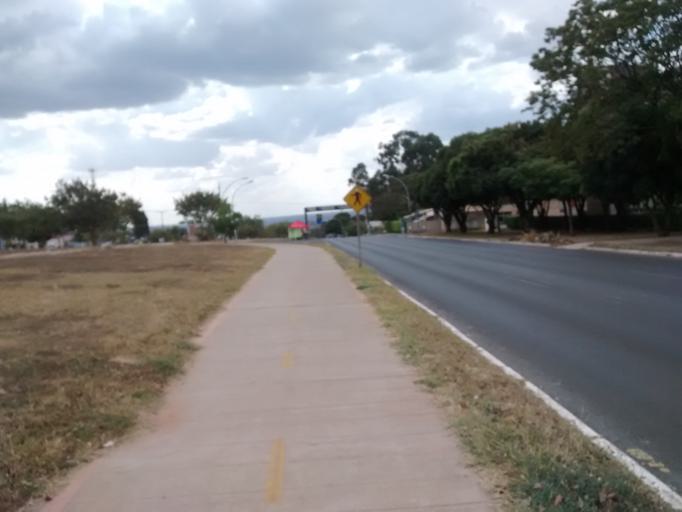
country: BR
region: Federal District
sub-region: Brasilia
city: Brasilia
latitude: -15.7498
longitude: -47.8986
